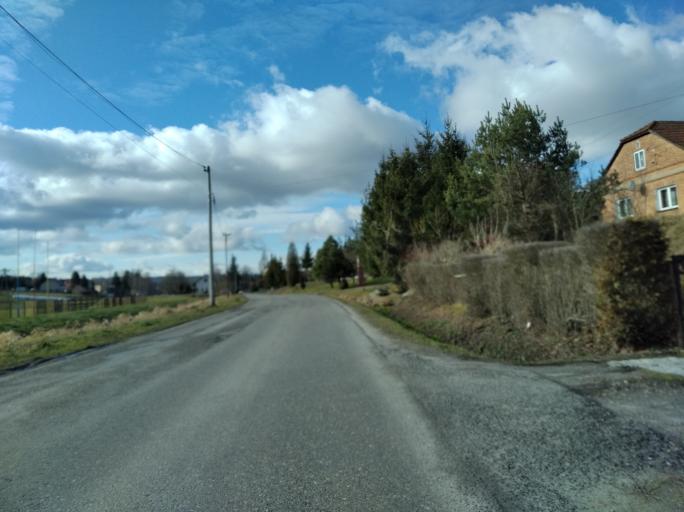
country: PL
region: Subcarpathian Voivodeship
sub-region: Powiat strzyzowski
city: Wisniowa
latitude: 49.9145
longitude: 21.7161
